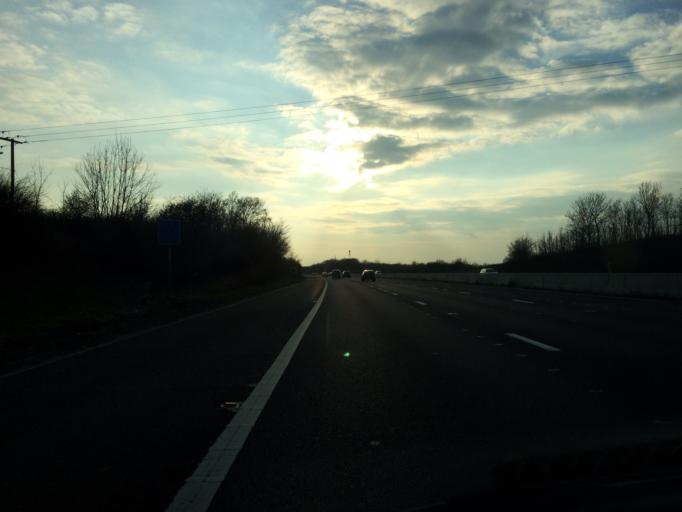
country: GB
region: England
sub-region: Wiltshire
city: Lyneham
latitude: 51.5471
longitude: -1.9572
